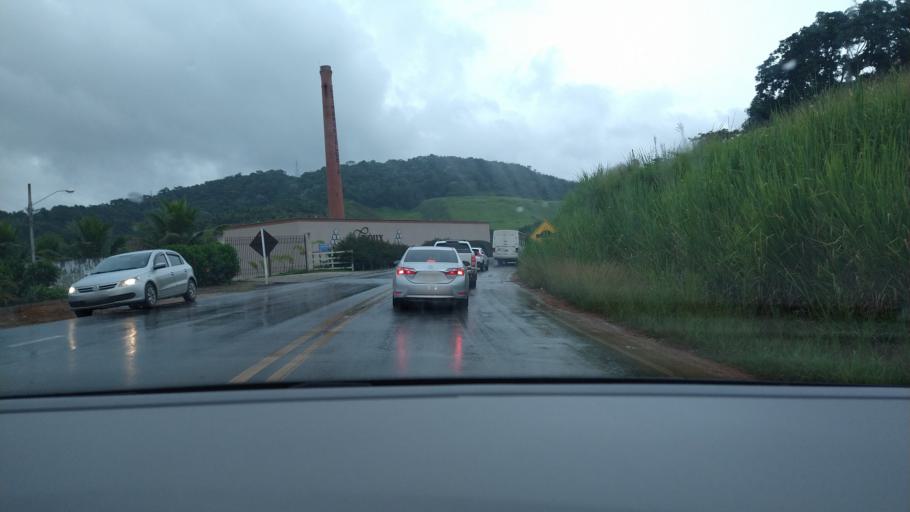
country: BR
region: Minas Gerais
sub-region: Vicosa
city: Vicosa
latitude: -20.6352
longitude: -42.8705
